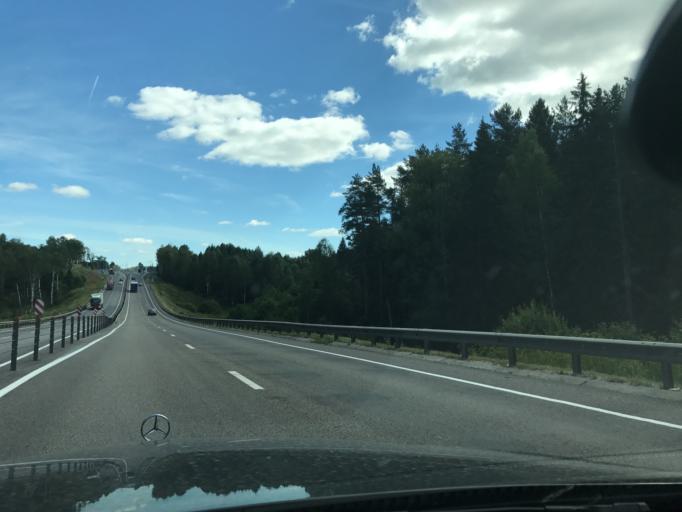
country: RU
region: Vladimir
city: Gorokhovets
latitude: 56.1681
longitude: 42.4540
